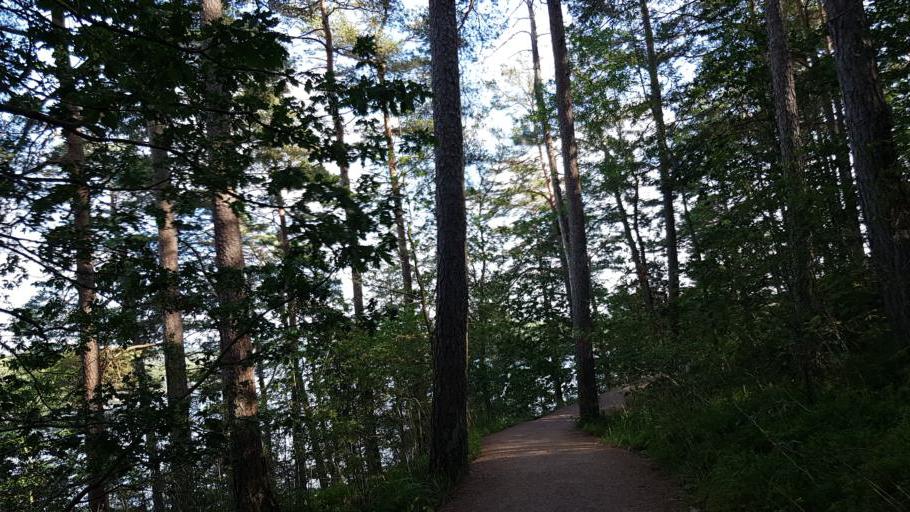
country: SE
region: Vaestra Goetaland
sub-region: Molndal
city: Moelndal
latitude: 57.6871
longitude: 12.0341
